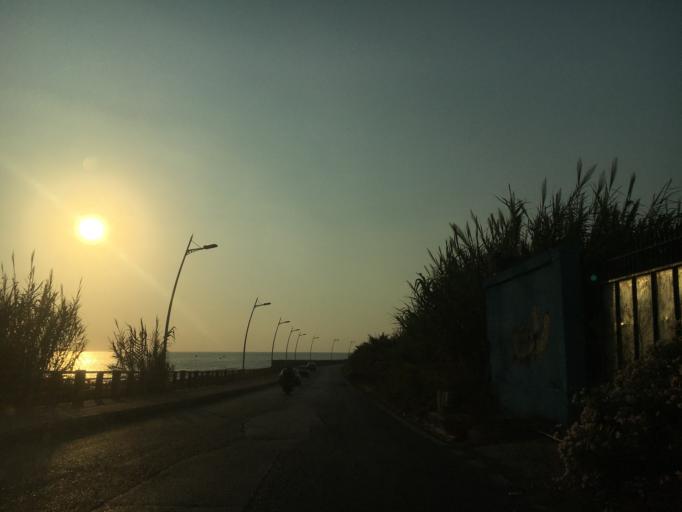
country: LB
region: Mont-Liban
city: Jbail
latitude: 34.1386
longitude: 35.6344
